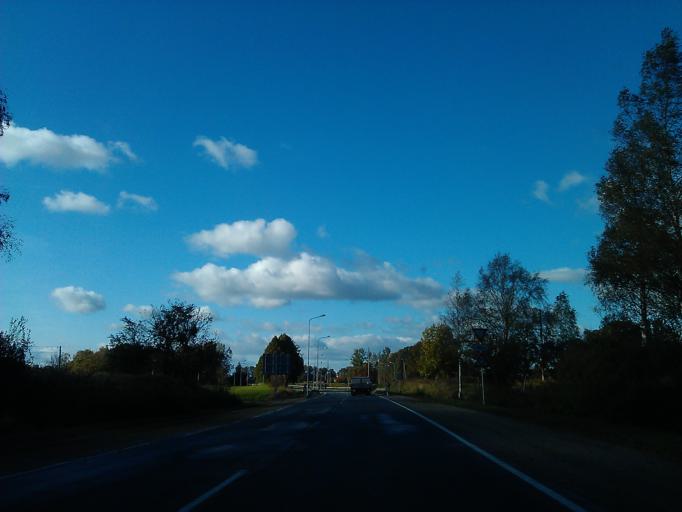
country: LV
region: Koknese
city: Koknese
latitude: 56.6396
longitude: 25.4488
